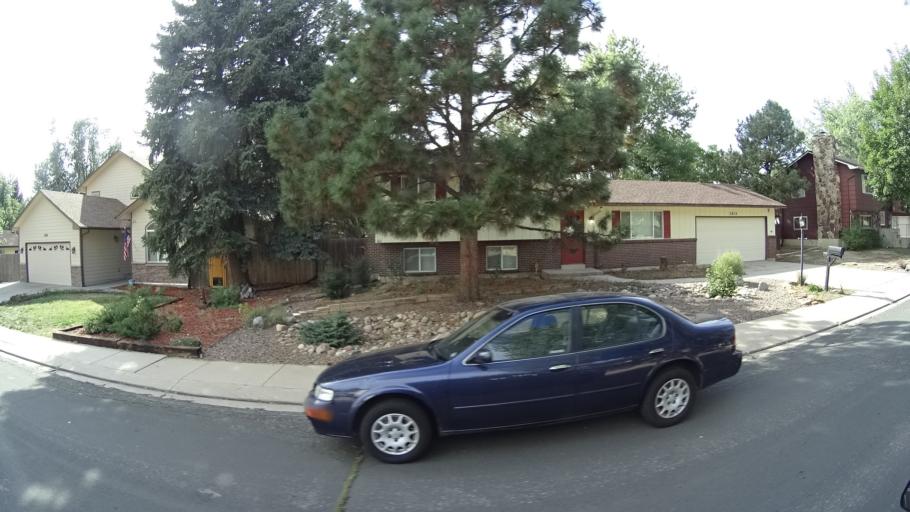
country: US
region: Colorado
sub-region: El Paso County
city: Colorado Springs
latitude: 38.8953
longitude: -104.7702
